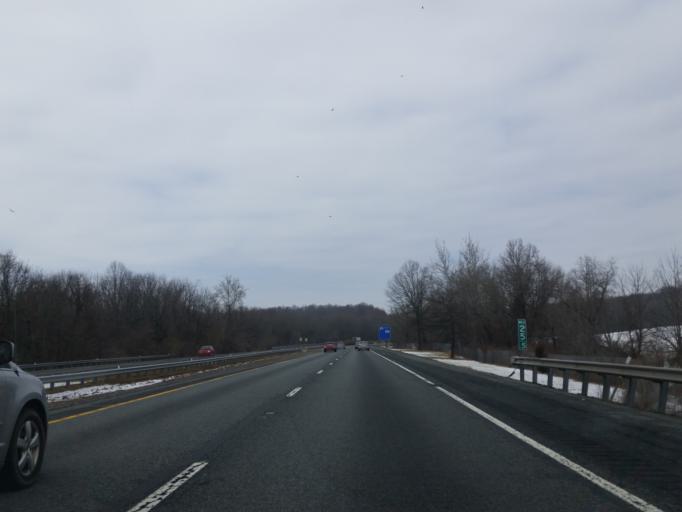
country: US
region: Maryland
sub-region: Baltimore County
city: Hunt Valley
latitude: 39.5679
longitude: -76.6690
